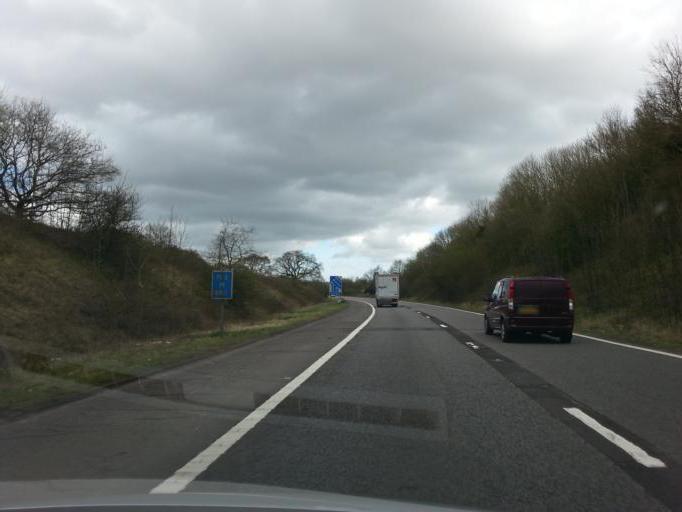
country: GB
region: England
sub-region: Hampshire
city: Overton
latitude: 51.2027
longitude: -1.1904
